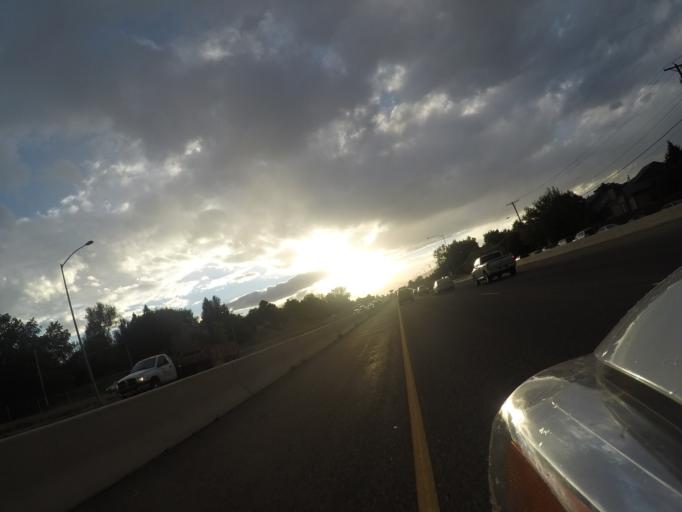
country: US
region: Colorado
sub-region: Arapahoe County
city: Sheridan
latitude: 39.6533
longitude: -105.0582
